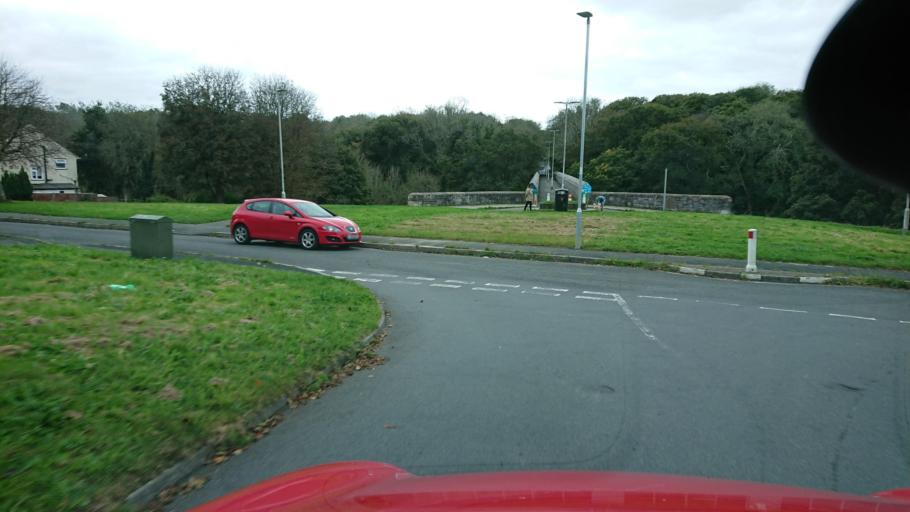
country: GB
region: England
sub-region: Plymouth
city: Plymouth
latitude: 50.4165
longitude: -4.1517
